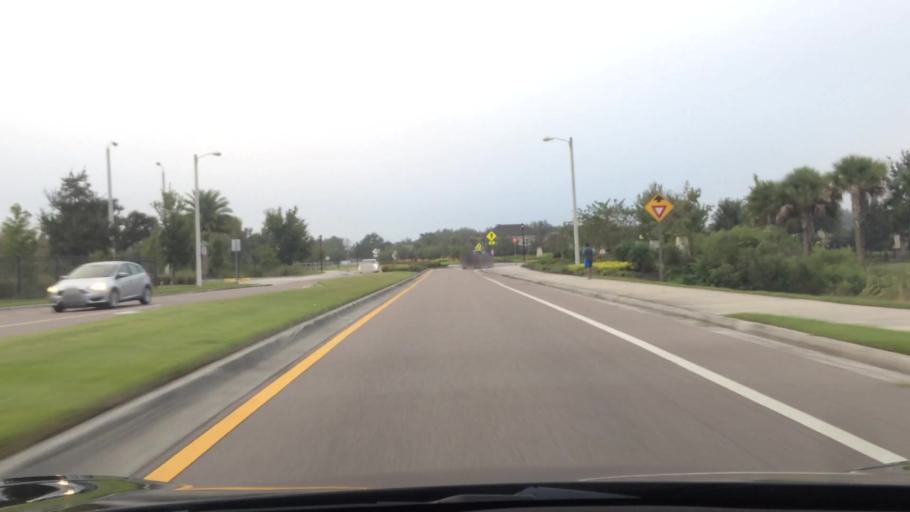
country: US
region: Florida
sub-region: Hillsborough County
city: Pebble Creek
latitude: 28.1834
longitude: -82.3666
